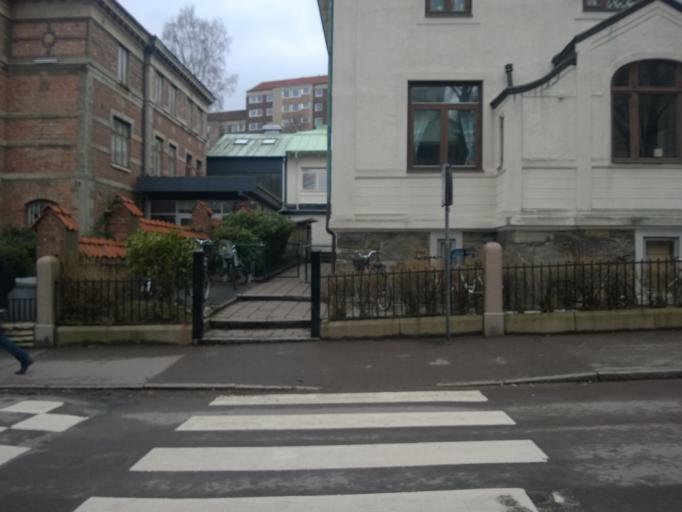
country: SE
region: Vaestra Goetaland
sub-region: Goteborg
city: Goeteborg
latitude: 57.6950
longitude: 11.9650
